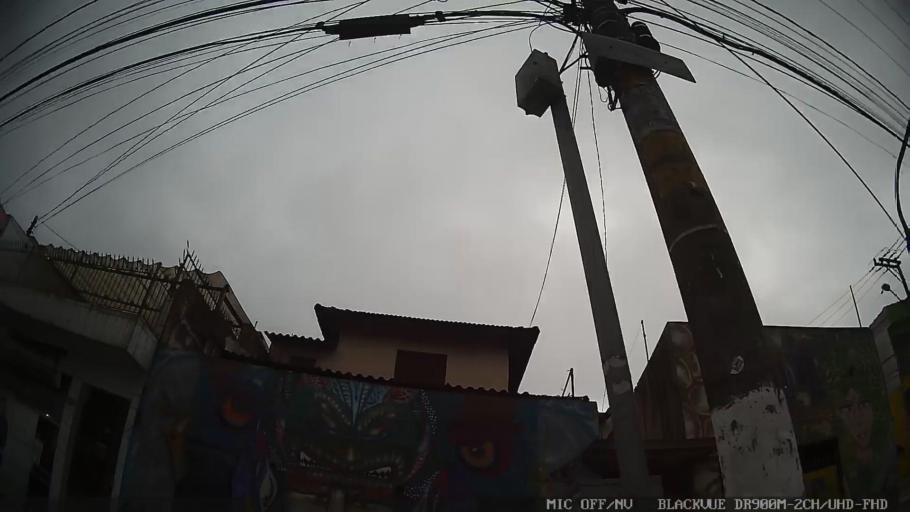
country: BR
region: Sao Paulo
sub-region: Osasco
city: Osasco
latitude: -23.4549
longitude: -46.7493
